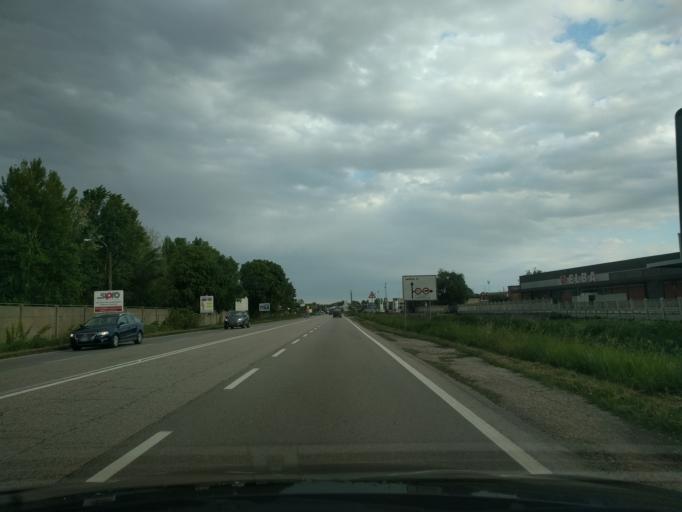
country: IT
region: Emilia-Romagna
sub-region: Provincia di Ferrara
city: Ferrara
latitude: 44.8553
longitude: 11.5844
